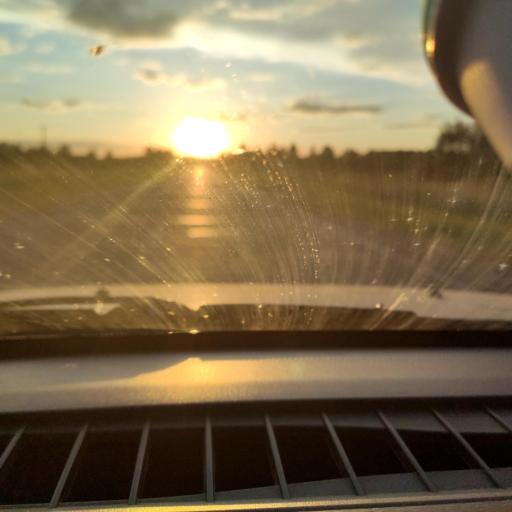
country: RU
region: Kirov
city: Kotel'nich
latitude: 58.5636
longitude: 48.1852
